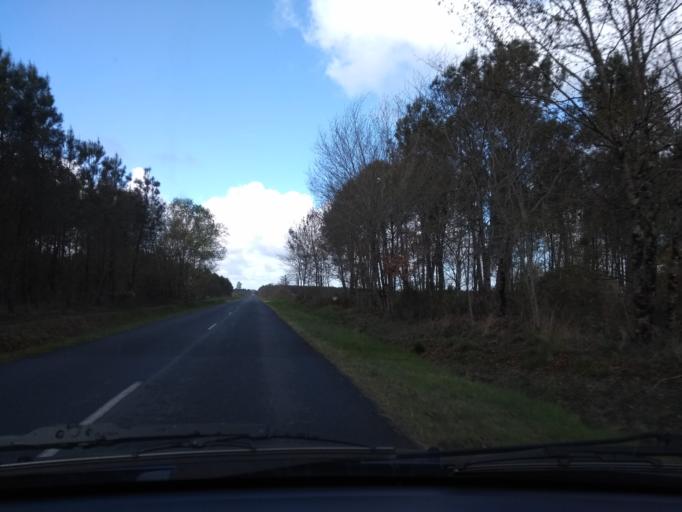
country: FR
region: Aquitaine
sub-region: Departement de la Gironde
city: Mios
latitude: 44.5507
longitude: -0.9570
